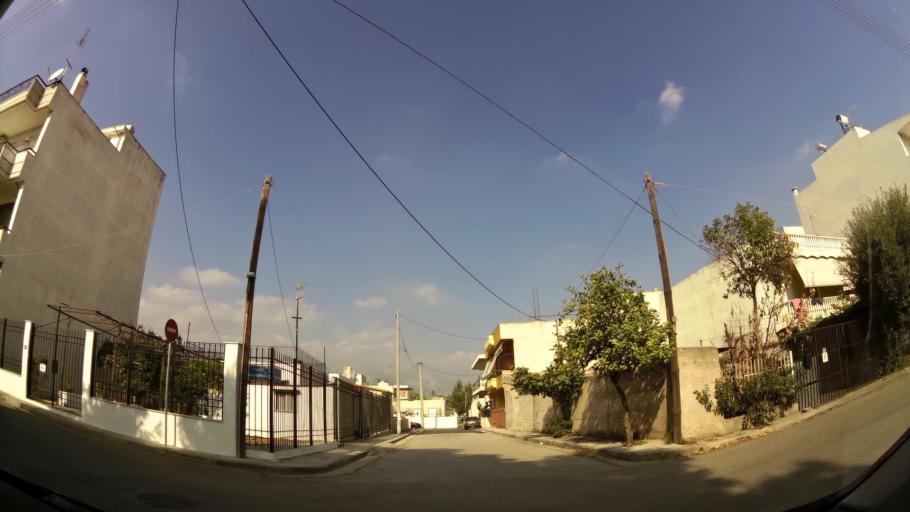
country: GR
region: Attica
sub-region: Nomarchia Dytikis Attikis
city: Zefyri
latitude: 38.0741
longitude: 23.7177
